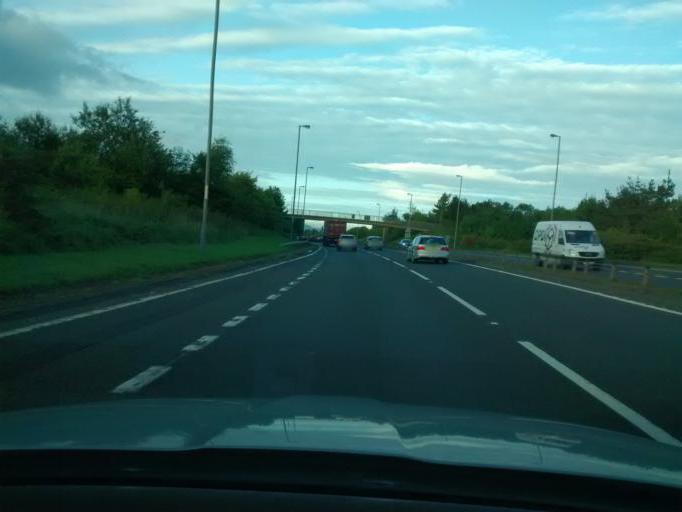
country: GB
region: Scotland
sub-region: Renfrewshire
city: Johnstone
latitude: 55.8340
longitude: -4.5291
